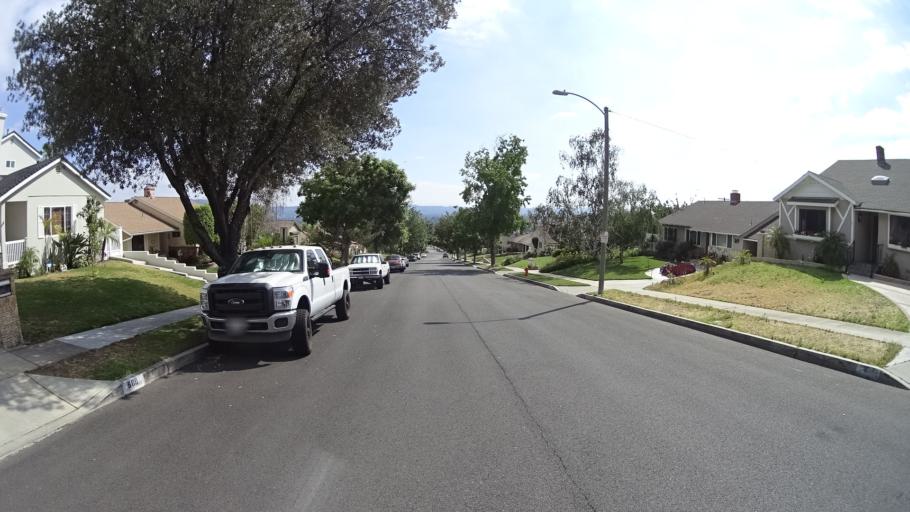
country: US
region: California
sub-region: Los Angeles County
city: Burbank
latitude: 34.2007
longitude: -118.3158
